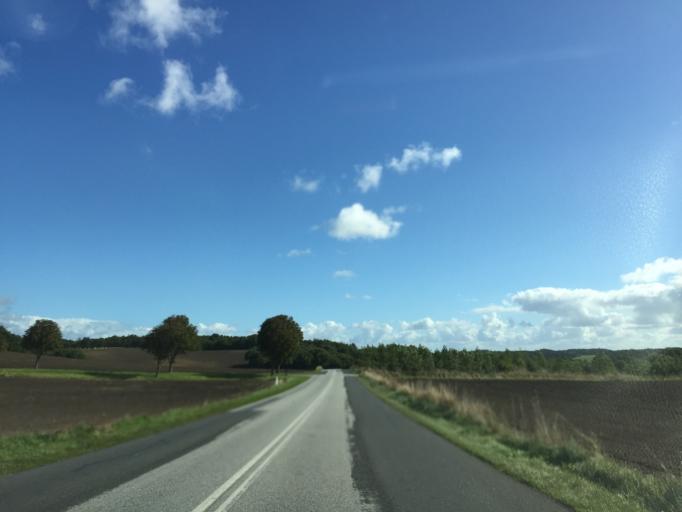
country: DK
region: Central Jutland
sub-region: Viborg Kommune
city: Viborg
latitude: 56.4418
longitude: 9.5016
